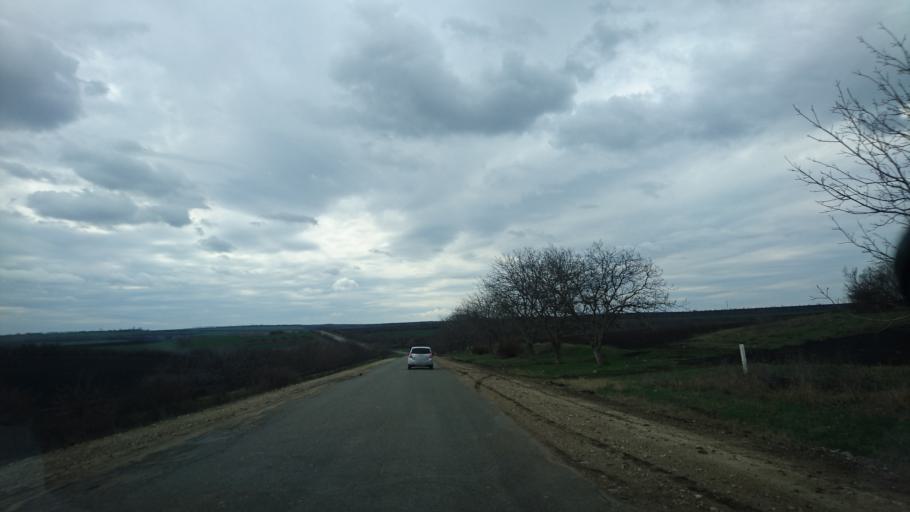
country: MD
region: Gagauzia
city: Comrat
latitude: 46.3105
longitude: 28.5909
